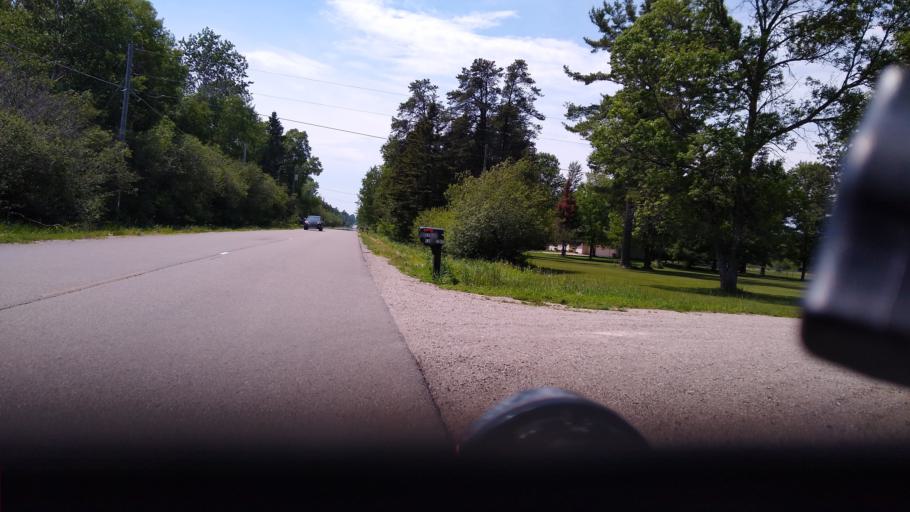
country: US
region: Michigan
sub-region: Delta County
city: Escanaba
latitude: 45.7099
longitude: -87.1016
